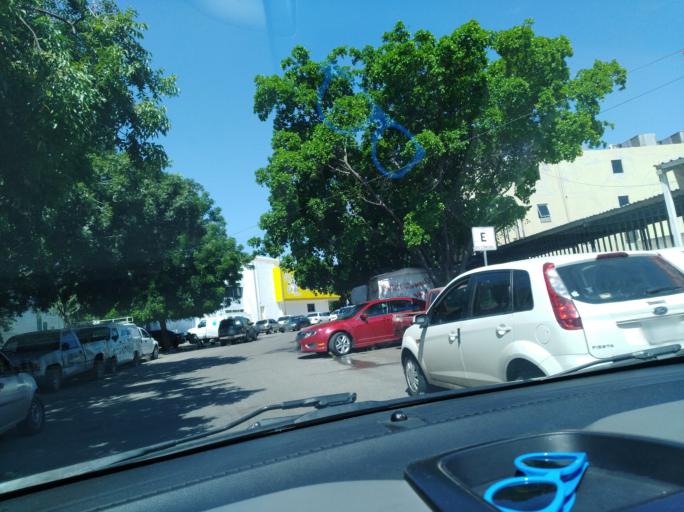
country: MX
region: Sinaloa
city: Culiacan
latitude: 24.7933
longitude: -107.4152
